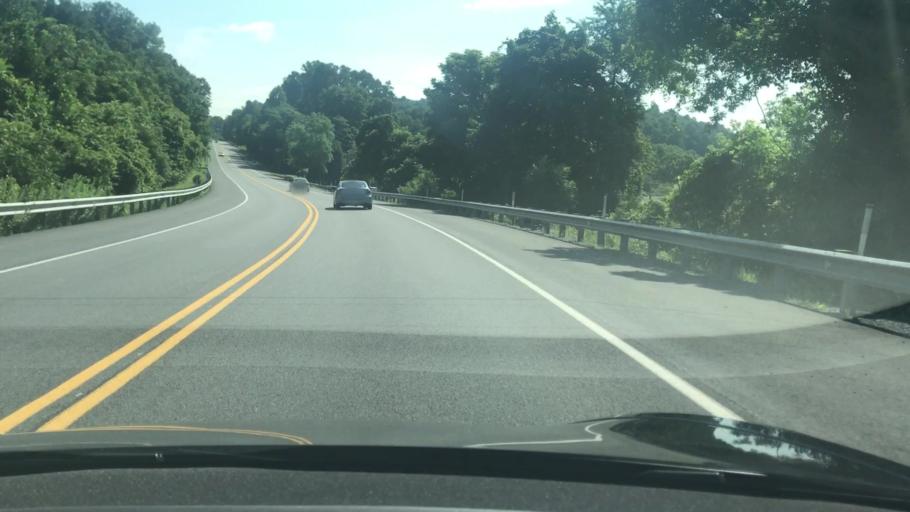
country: US
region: Pennsylvania
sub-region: York County
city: Valley Green
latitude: 40.1309
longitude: -76.8180
